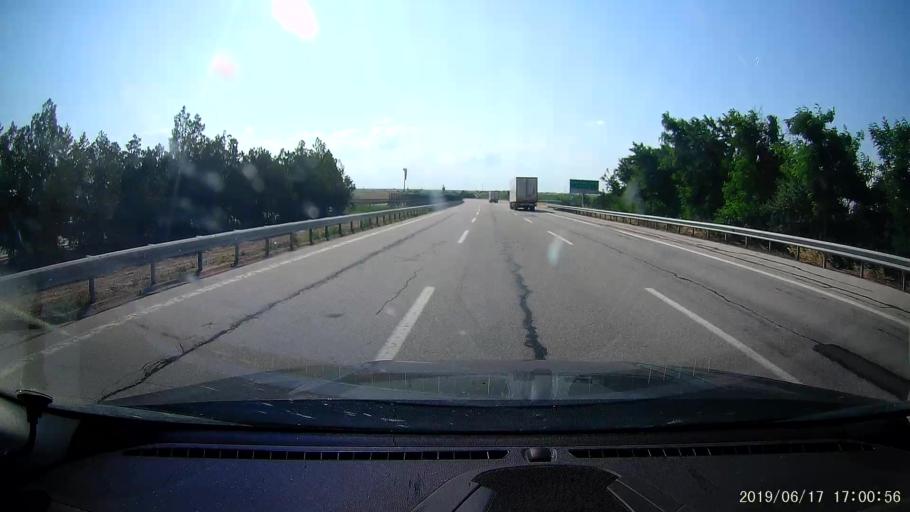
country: TR
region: Edirne
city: Haskoy
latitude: 41.6256
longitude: 26.8174
